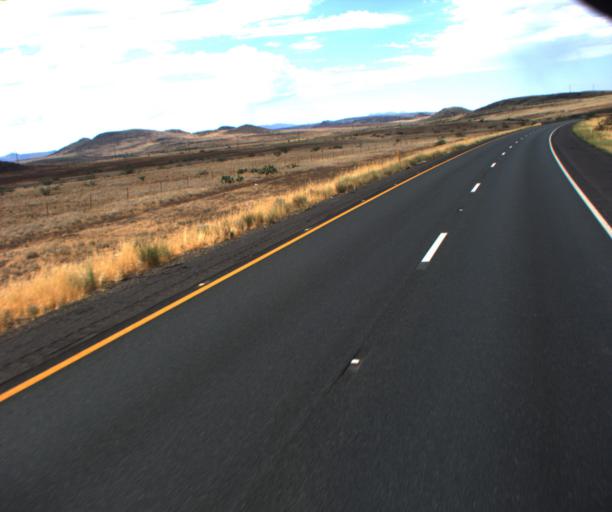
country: US
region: Arizona
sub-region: Yavapai County
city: Cordes Lakes
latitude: 34.4508
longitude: -112.0350
